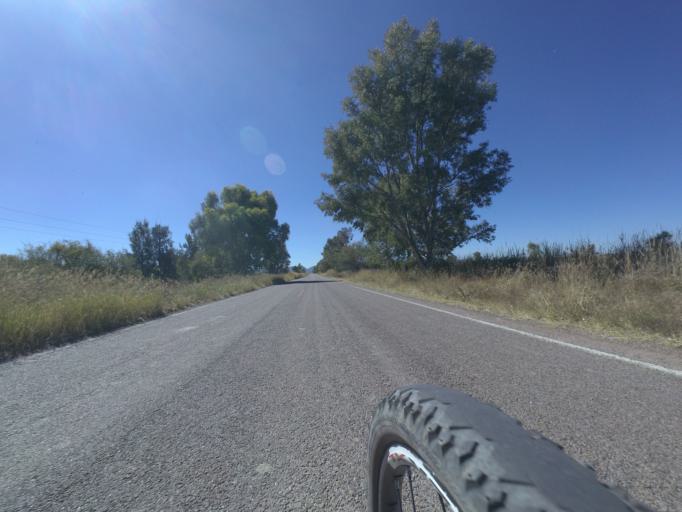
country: MX
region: Aguascalientes
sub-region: Aguascalientes
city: Los Canos
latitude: 21.8725
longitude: -102.4976
